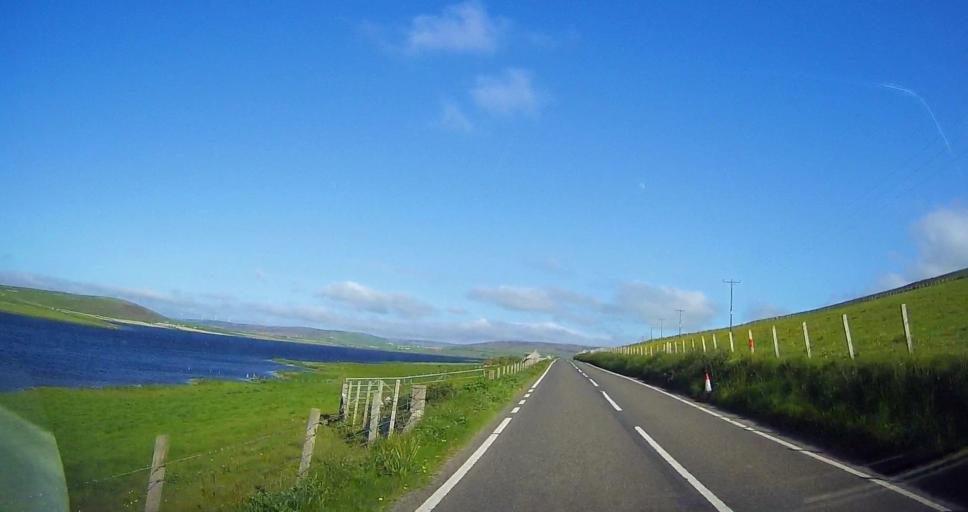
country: GB
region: Scotland
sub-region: Orkney Islands
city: Stromness
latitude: 59.1144
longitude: -3.2998
